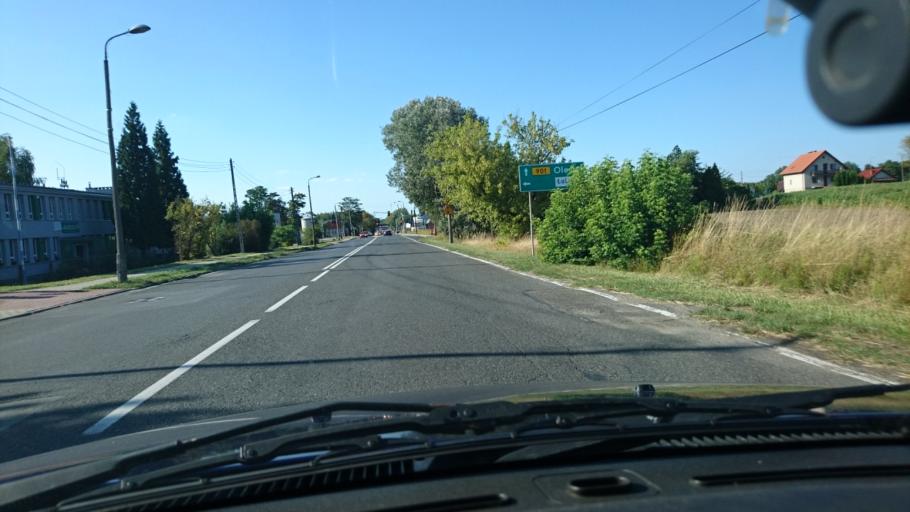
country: PL
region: Silesian Voivodeship
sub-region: Powiat gliwicki
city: Pyskowice
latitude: 50.3627
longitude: 18.6401
